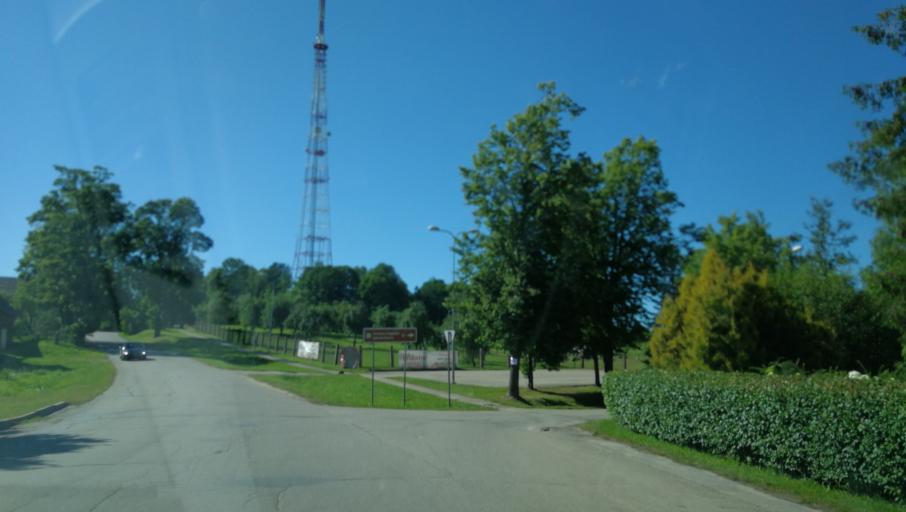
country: LV
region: Cesvaine
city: Cesvaine
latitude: 56.9688
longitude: 26.3051
